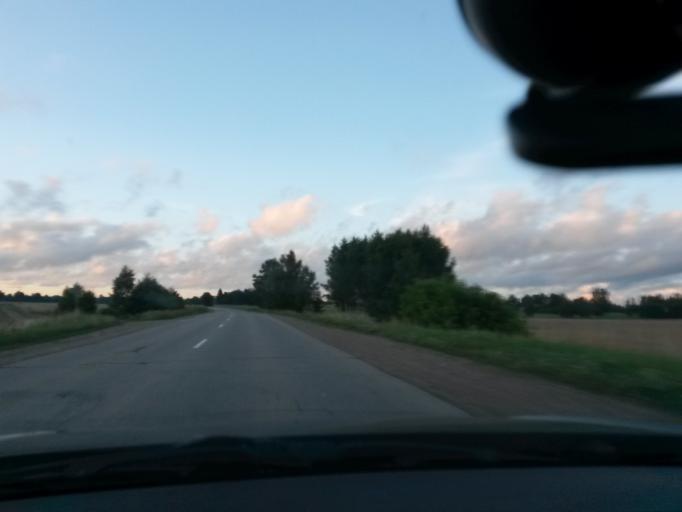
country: LV
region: Madonas Rajons
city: Madona
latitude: 56.7373
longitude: 26.0170
